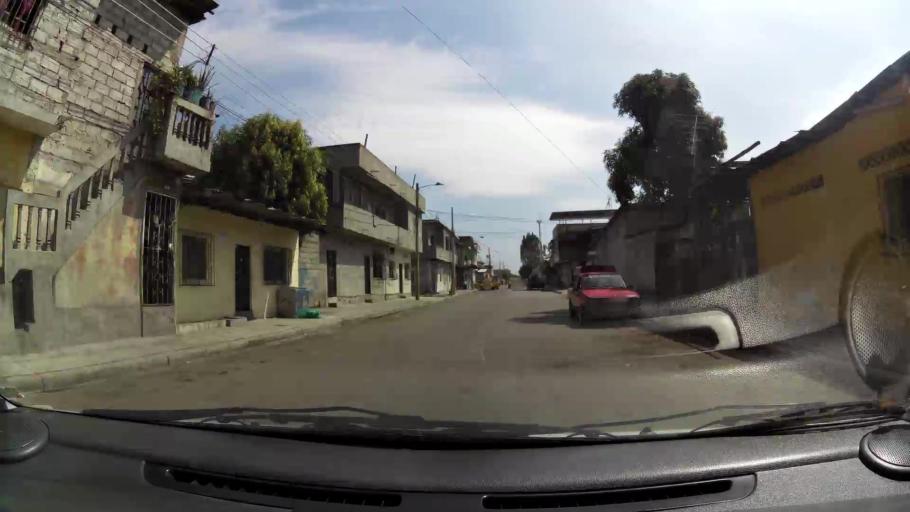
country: EC
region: Guayas
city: Guayaquil
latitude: -2.2677
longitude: -79.8836
